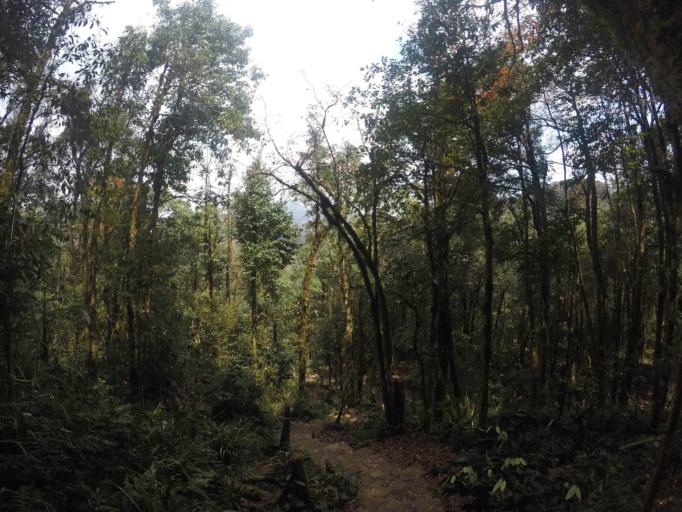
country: VN
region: Lao Cai
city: Sa Pa
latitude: 22.3488
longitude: 103.7744
